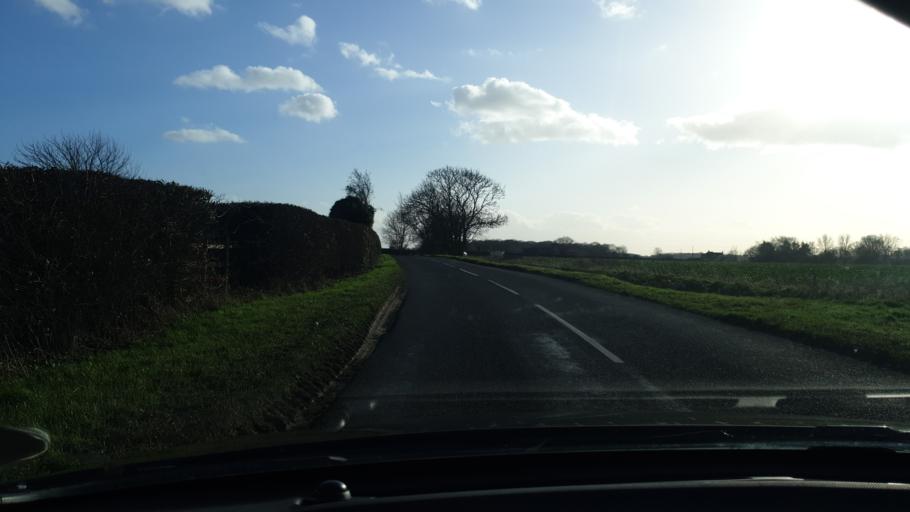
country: GB
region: England
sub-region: Essex
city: Mistley
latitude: 51.9030
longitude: 1.1430
